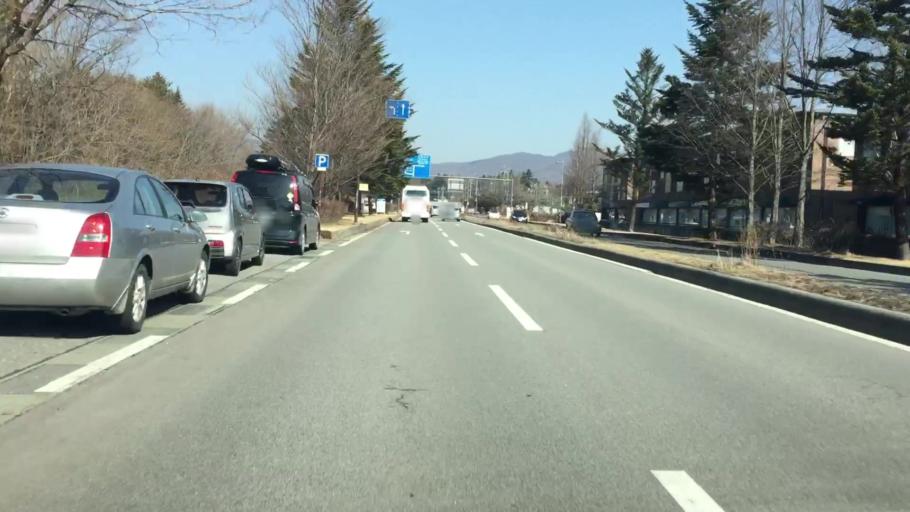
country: JP
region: Nagano
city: Saku
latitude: 36.3400
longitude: 138.6308
